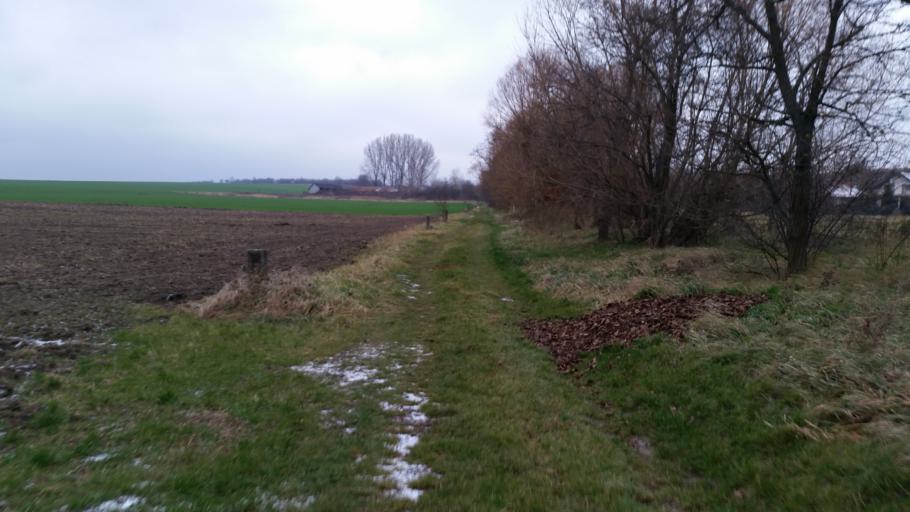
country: HU
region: Pest
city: Telki
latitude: 47.5574
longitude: 18.7961
